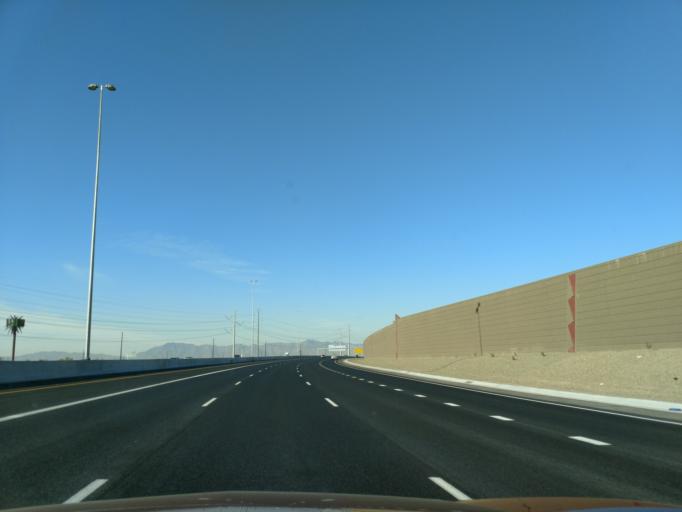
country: US
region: Arizona
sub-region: Maricopa County
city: Guadalupe
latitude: 33.2928
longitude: -111.9861
